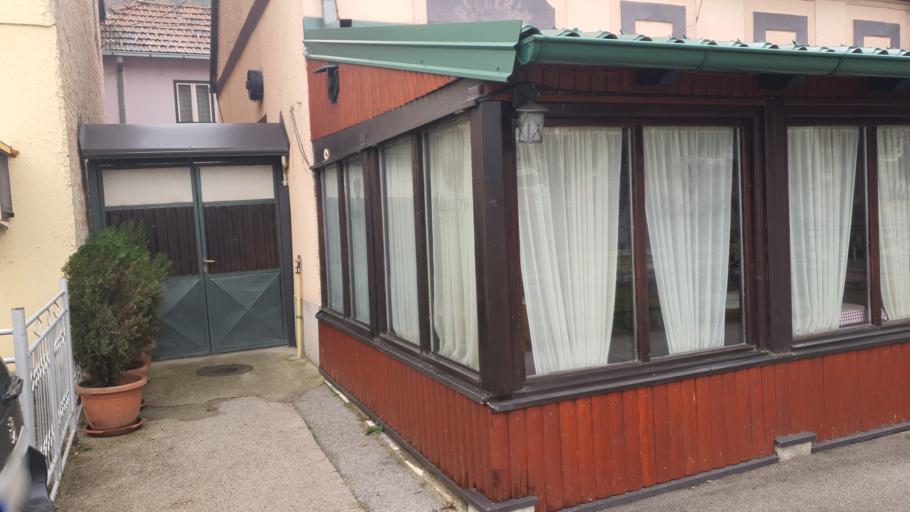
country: RS
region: Central Serbia
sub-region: Zlatiborski Okrug
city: Uzice
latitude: 43.8516
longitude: 19.8439
